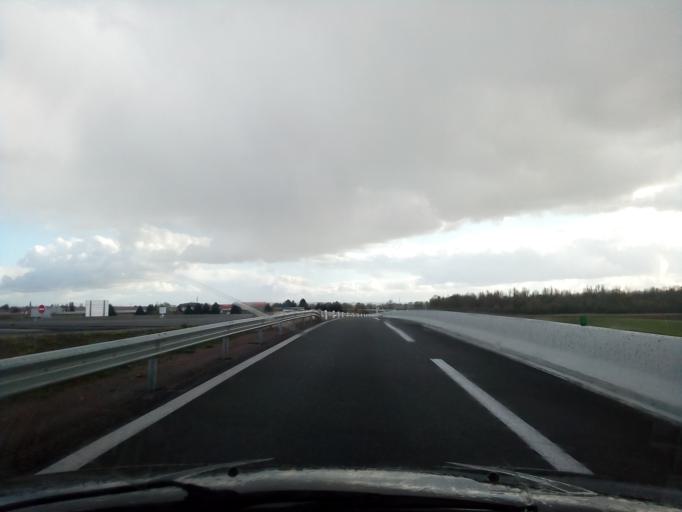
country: FR
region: Auvergne
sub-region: Departement de l'Allier
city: Varennes-sur-Allier
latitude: 46.3230
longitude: 3.3799
